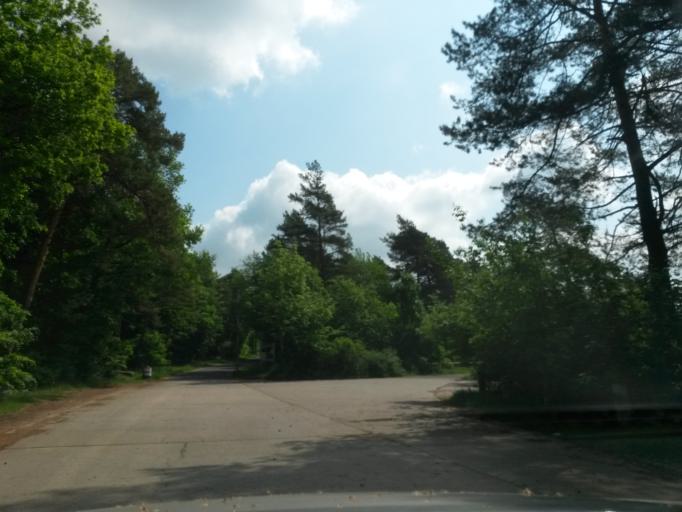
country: DE
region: Bavaria
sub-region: Regierungsbezirk Unterfranken
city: Nudlingen
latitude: 50.1994
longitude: 10.1068
